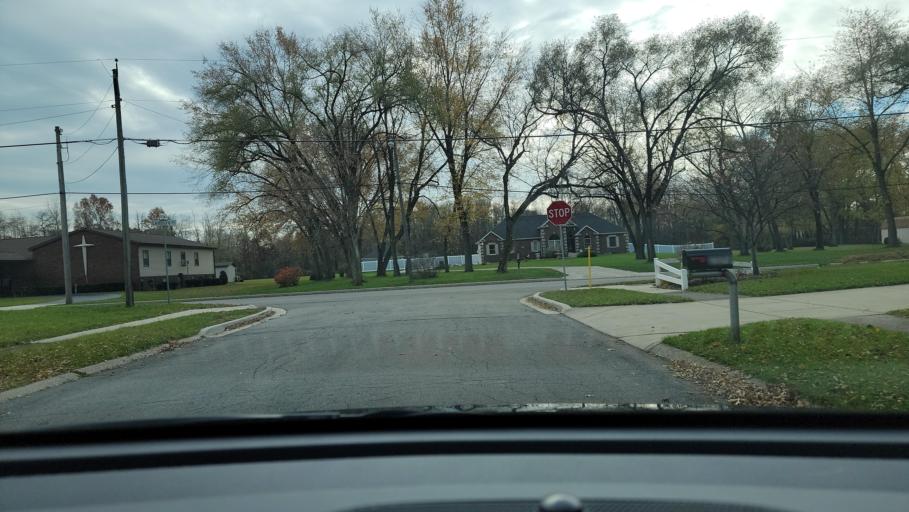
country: US
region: Indiana
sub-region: Porter County
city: Portage
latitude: 41.5831
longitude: -87.1418
